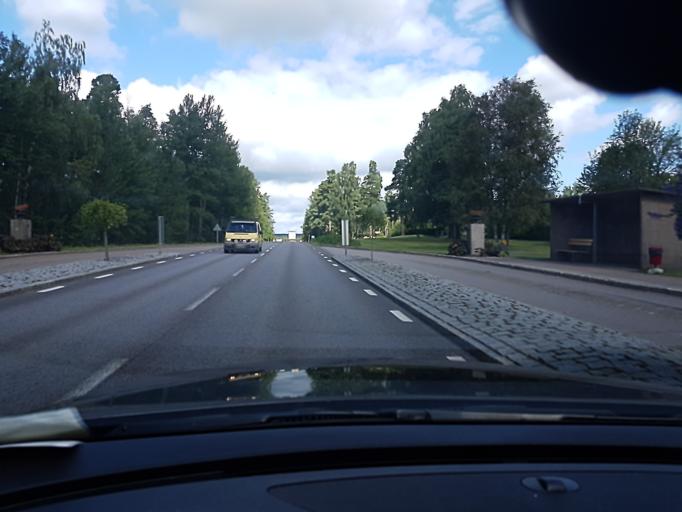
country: SE
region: Kronoberg
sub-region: Lessebo Kommun
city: Lessebo
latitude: 56.7622
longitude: 15.2655
